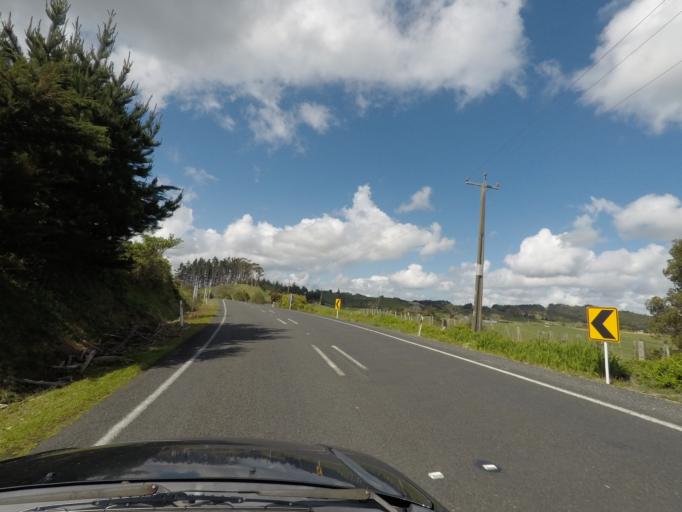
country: NZ
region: Auckland
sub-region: Auckland
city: Pukekohe East
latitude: -37.1441
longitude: 175.0119
